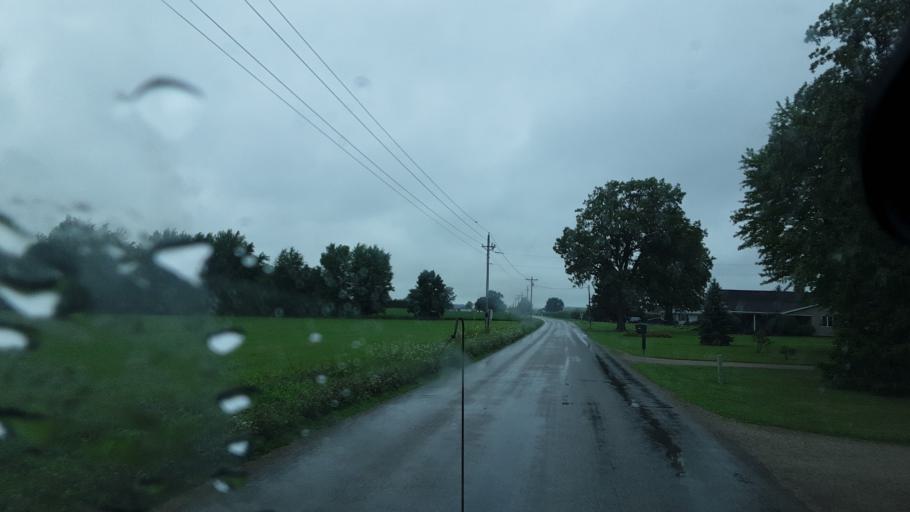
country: US
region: Indiana
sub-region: Adams County
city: Berne
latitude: 40.7199
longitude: -84.8533
